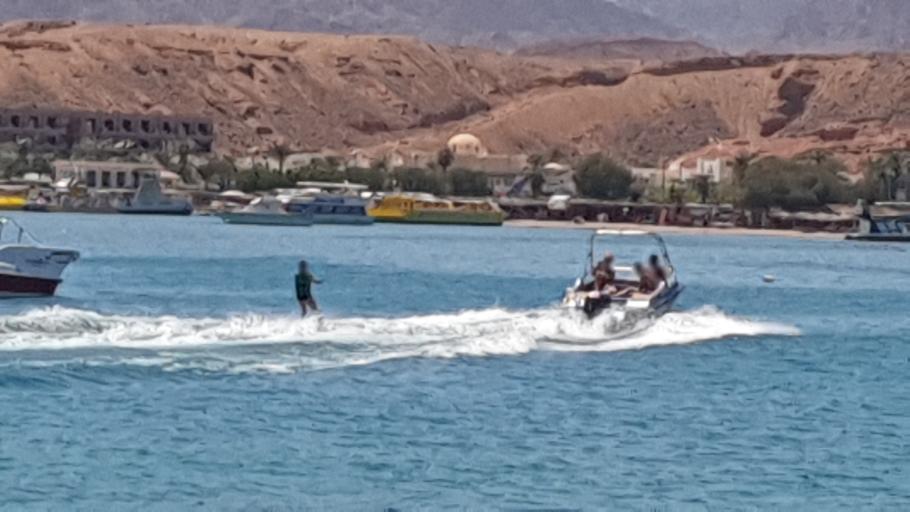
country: EG
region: South Sinai
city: Sharm el-Sheikh
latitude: 27.8600
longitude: 34.2975
